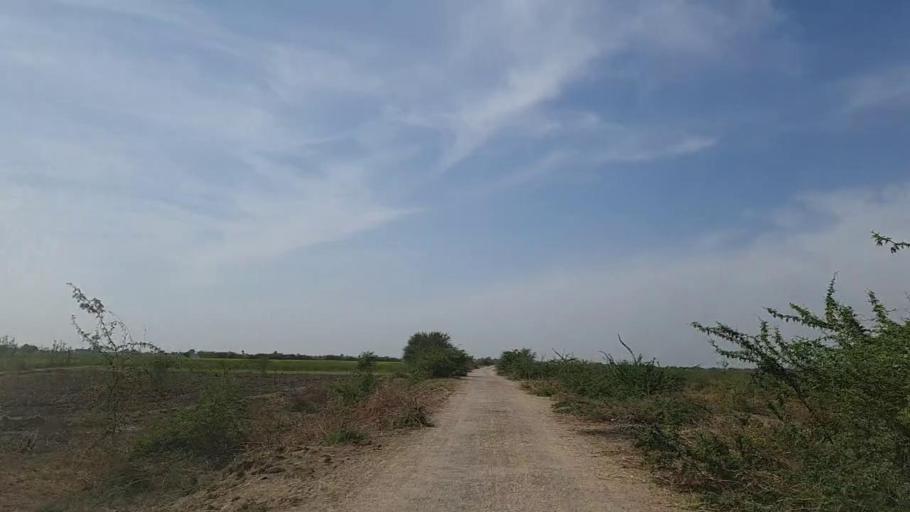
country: PK
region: Sindh
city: Samaro
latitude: 25.2060
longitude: 69.4484
